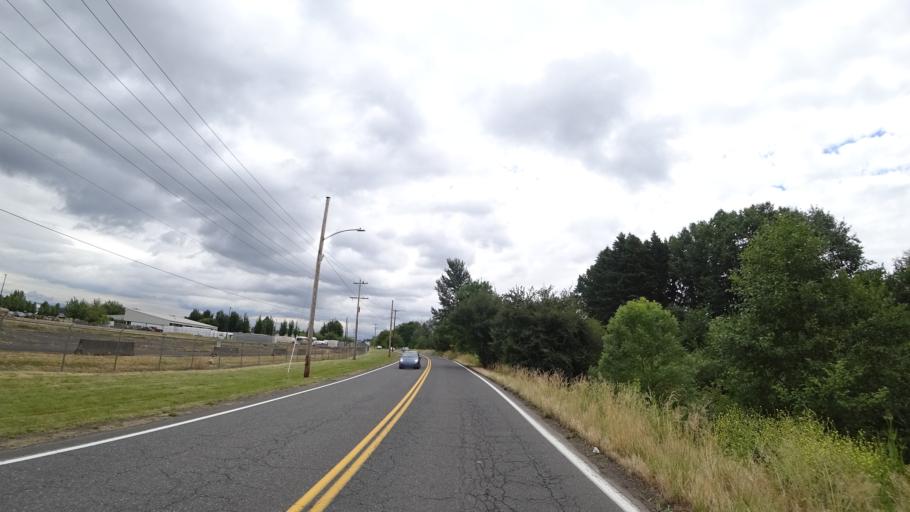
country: US
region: Washington
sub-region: Clark County
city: Vancouver
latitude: 45.5745
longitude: -122.5978
